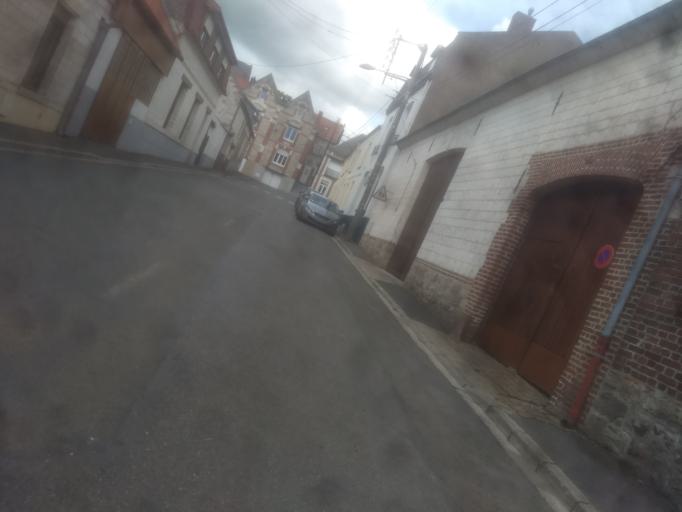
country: FR
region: Nord-Pas-de-Calais
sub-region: Departement du Pas-de-Calais
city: Maroeuil
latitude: 50.3242
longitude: 2.7036
